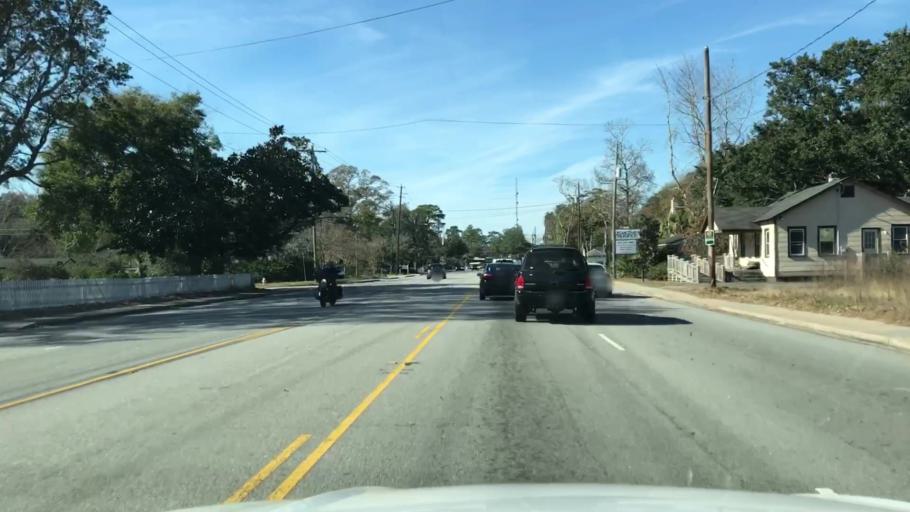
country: US
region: South Carolina
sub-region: Charleston County
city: North Charleston
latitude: 32.7997
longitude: -80.0113
